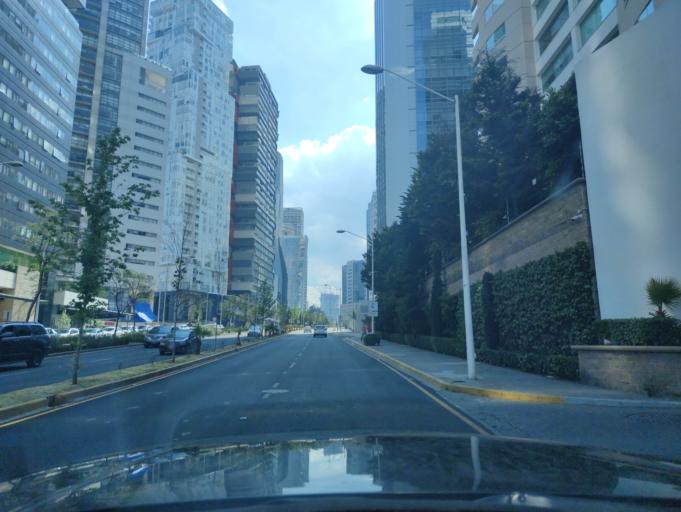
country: MX
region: Mexico City
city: Col. Bosques de las Lomas
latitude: 19.3599
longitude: -99.2702
